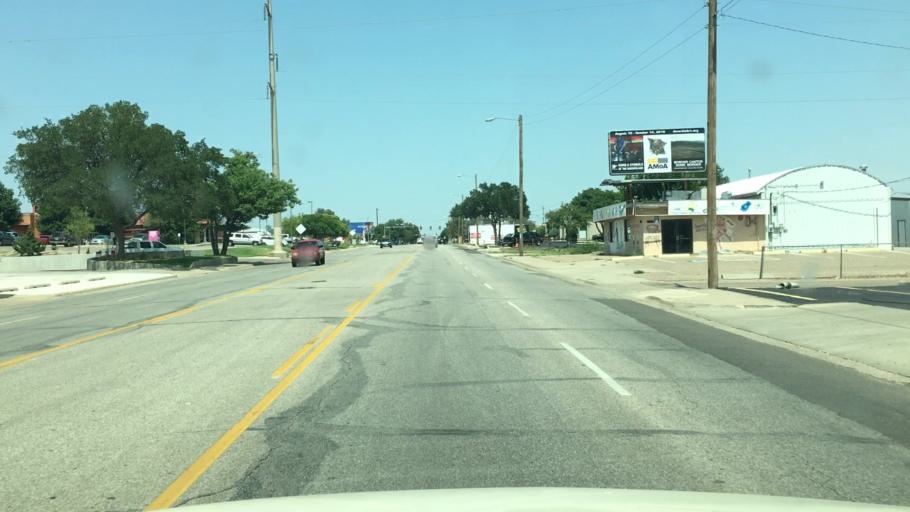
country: US
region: Texas
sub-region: Potter County
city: Amarillo
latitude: 35.1979
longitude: -101.8166
